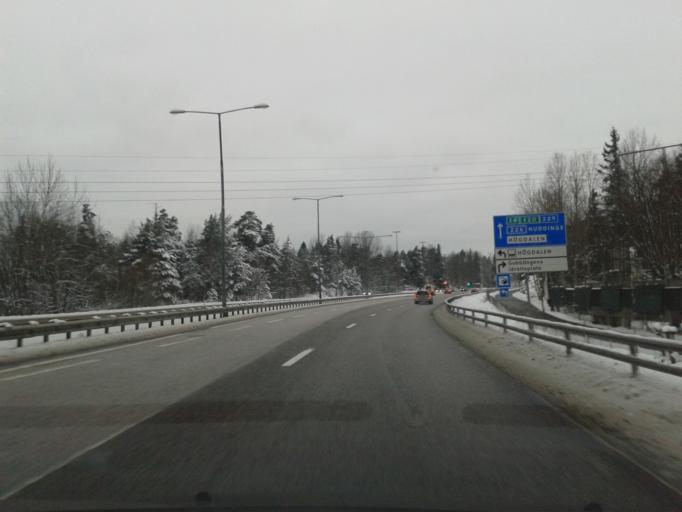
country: SE
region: Stockholm
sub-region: Stockholms Kommun
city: Arsta
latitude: 59.2613
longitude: 18.0670
